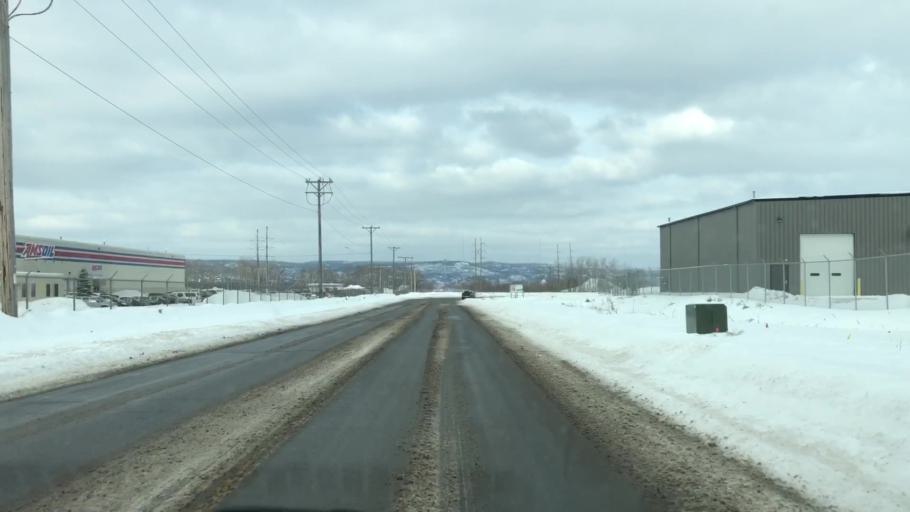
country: US
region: Wisconsin
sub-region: Douglas County
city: Superior
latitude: 46.7253
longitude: -92.1257
